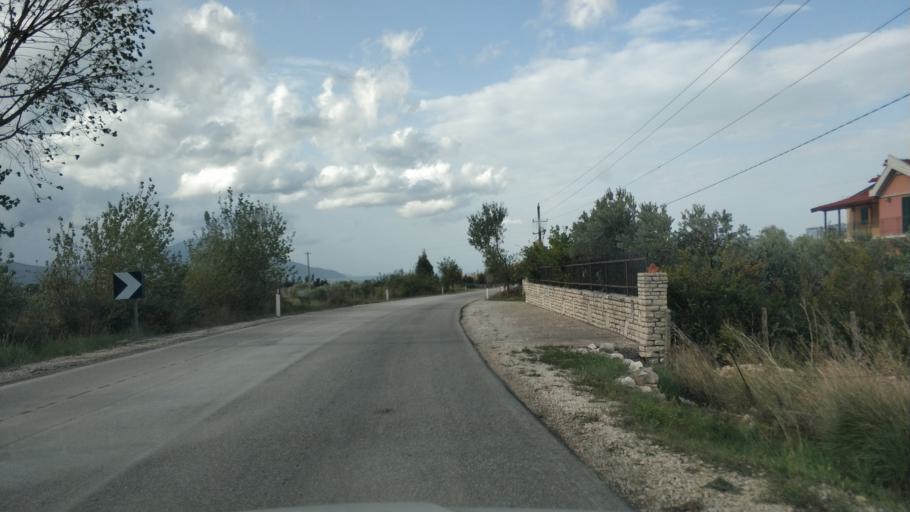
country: AL
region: Vlore
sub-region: Rrethi i Vlores
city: Orikum
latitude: 40.2886
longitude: 19.4936
